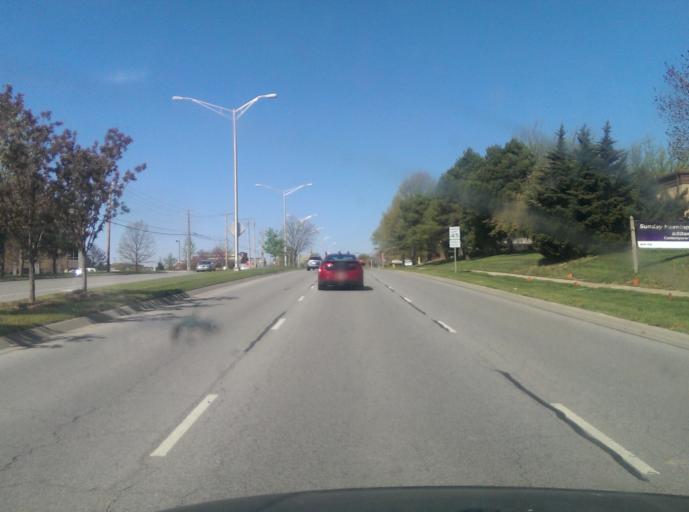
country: US
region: Kansas
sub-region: Johnson County
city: Lenexa
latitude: 38.9275
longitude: -94.7145
